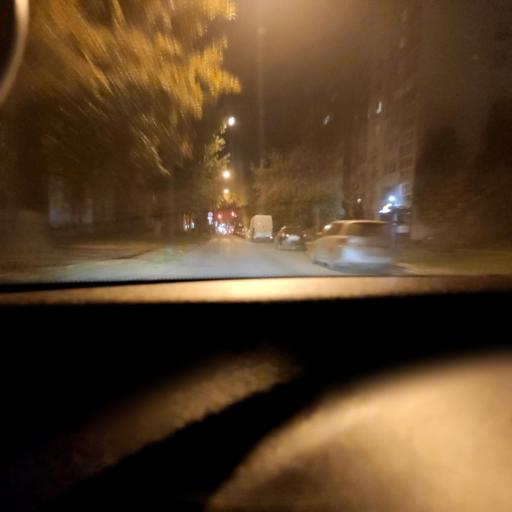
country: RU
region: Samara
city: Samara
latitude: 53.2167
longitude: 50.2475
